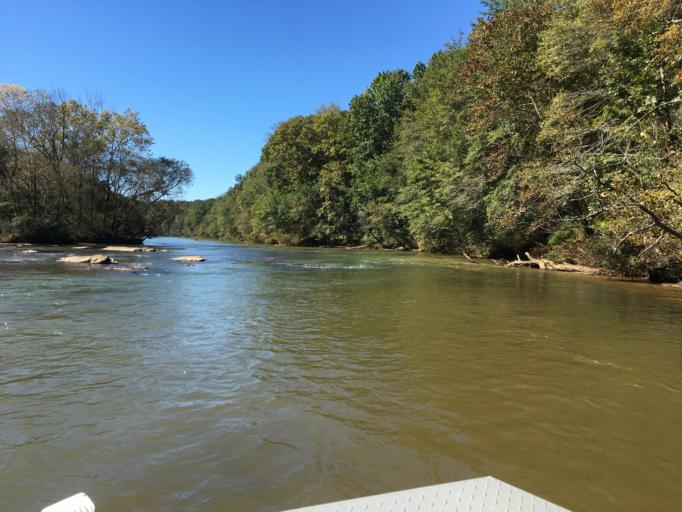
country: US
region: Georgia
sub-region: Fulton County
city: Johns Creek
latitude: 34.0000
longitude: -84.2393
